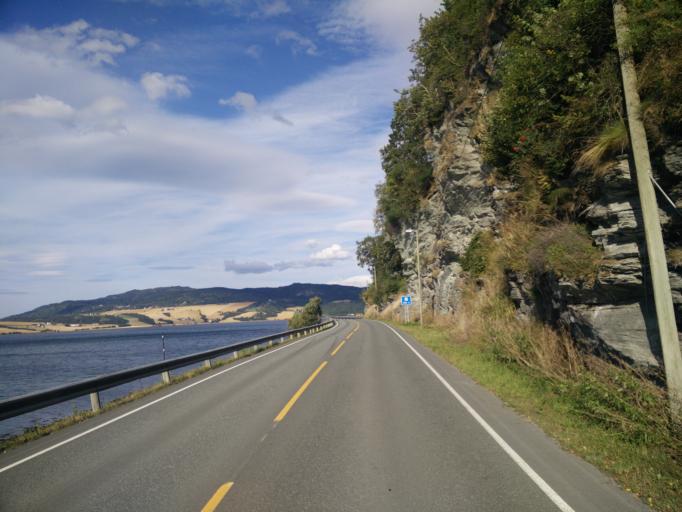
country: NO
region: Sor-Trondelag
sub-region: Melhus
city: Melhus
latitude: 63.3198
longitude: 10.1936
